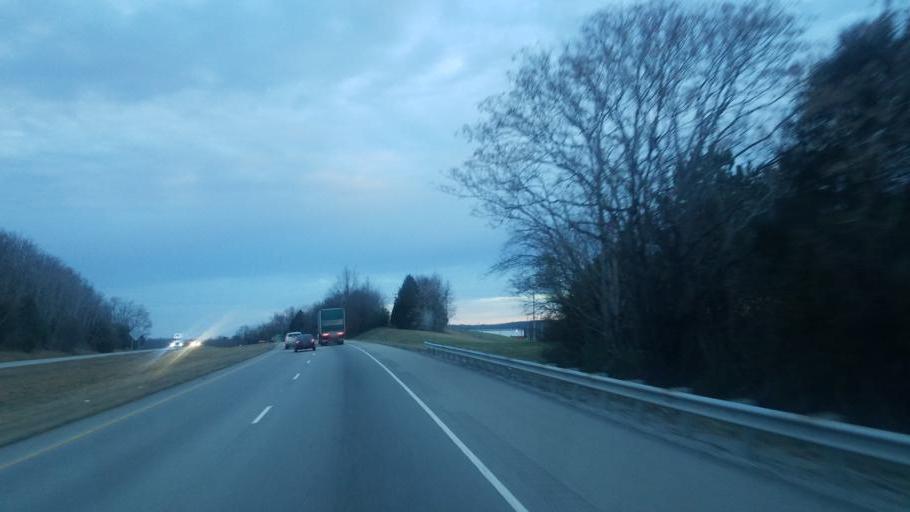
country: US
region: Tennessee
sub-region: White County
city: Sparta
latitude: 35.9474
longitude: -85.4834
